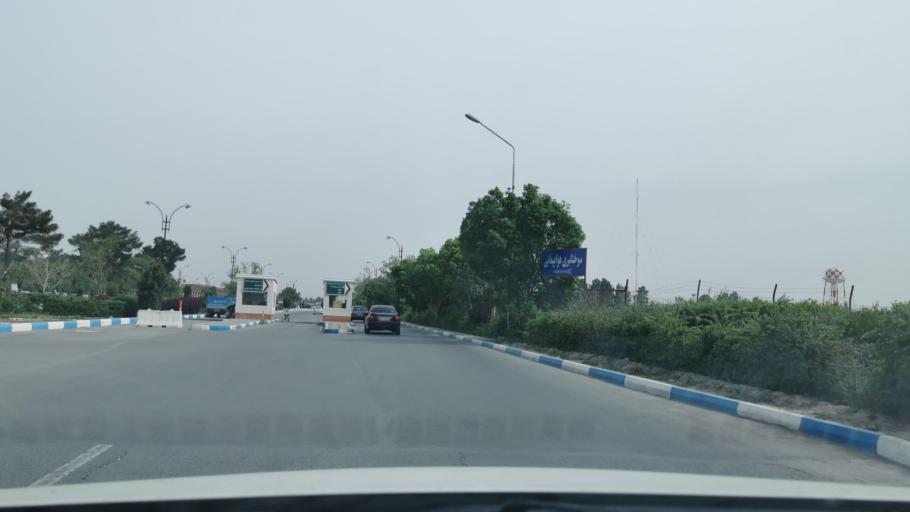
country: IR
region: Razavi Khorasan
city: Mashhad
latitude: 36.2299
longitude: 59.6372
